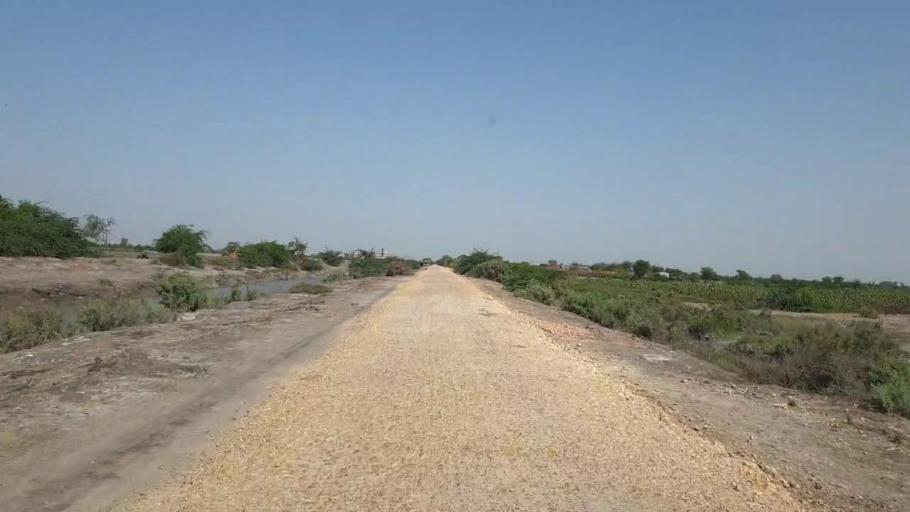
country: PK
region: Sindh
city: Tando Bago
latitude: 24.7309
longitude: 69.0740
